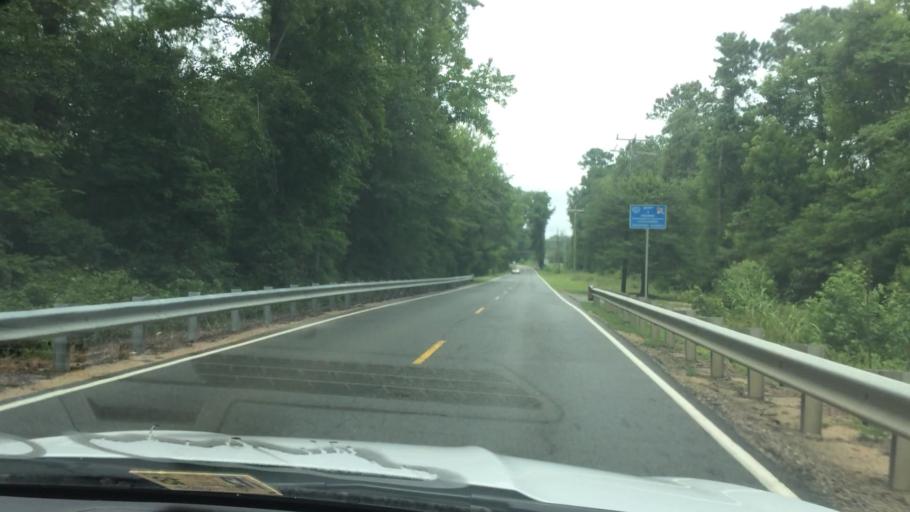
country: US
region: Virginia
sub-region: Charles City County
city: Charles City
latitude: 37.4292
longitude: -77.0384
